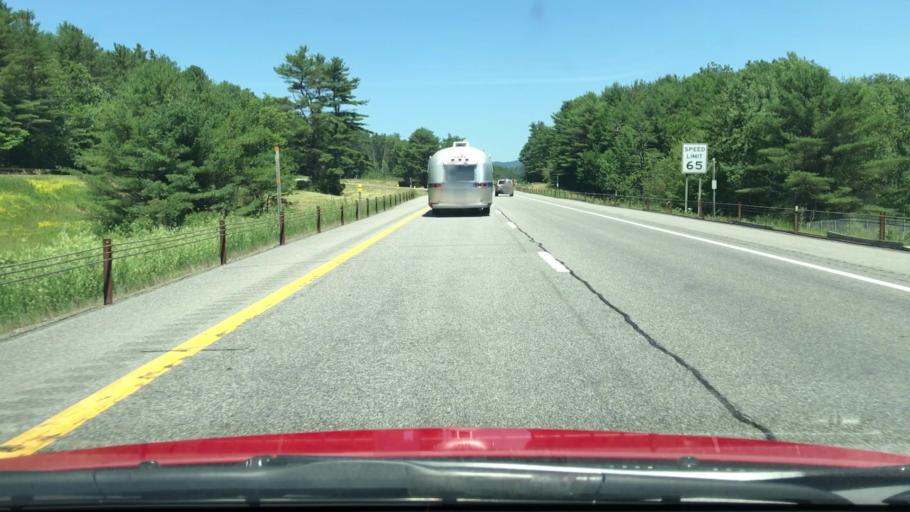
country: US
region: New York
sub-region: Essex County
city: Elizabethtown
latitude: 44.2949
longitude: -73.5316
